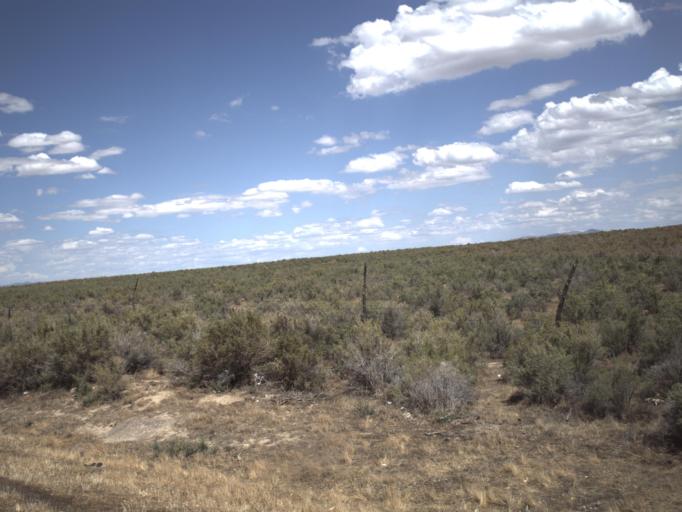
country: US
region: Utah
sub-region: Millard County
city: Delta
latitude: 39.3433
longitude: -112.4935
